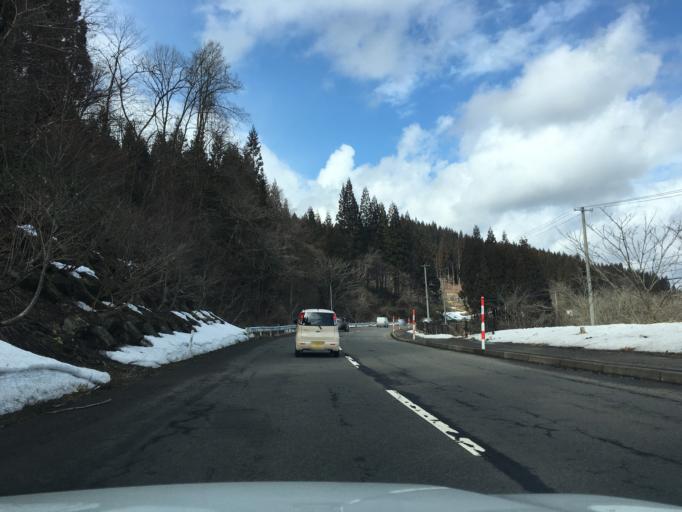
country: JP
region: Akita
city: Takanosu
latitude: 40.0148
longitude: 140.2774
